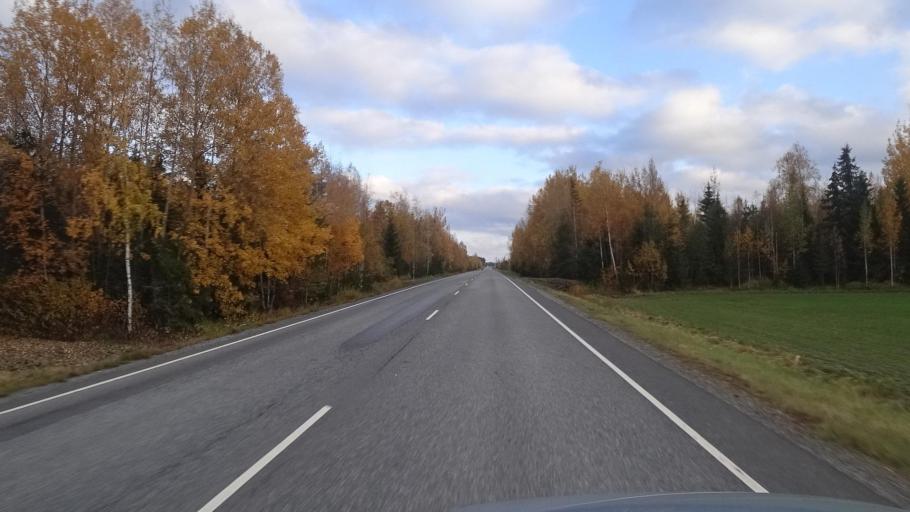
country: FI
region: Varsinais-Suomi
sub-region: Loimaa
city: Alastaro
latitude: 60.9060
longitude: 22.9267
